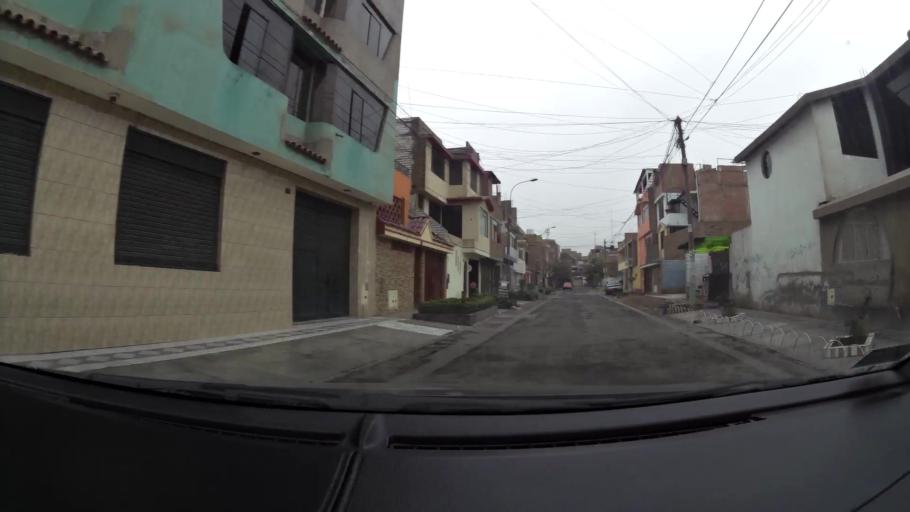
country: PE
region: Lima
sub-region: Lima
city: Independencia
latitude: -11.9740
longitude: -77.0838
